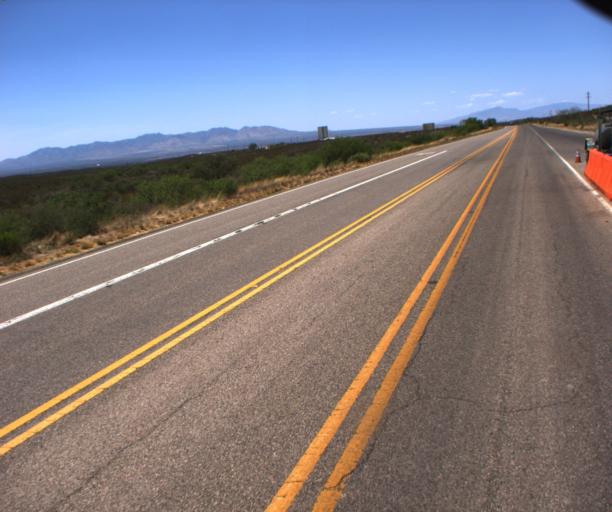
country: US
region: Arizona
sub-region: Cochise County
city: Tombstone
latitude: 31.7491
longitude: -110.0976
